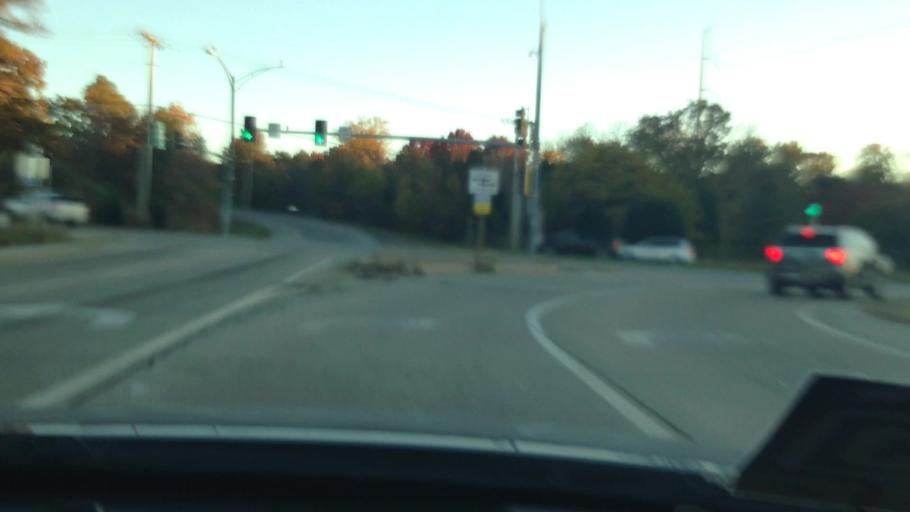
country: US
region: Kansas
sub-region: Johnson County
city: Lenexa
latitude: 38.9134
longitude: -94.7005
